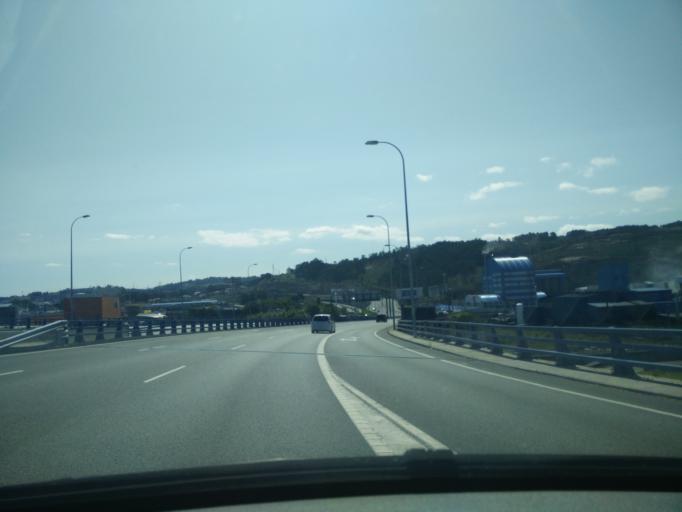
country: ES
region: Galicia
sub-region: Provincia da Coruna
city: A Coruna
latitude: 43.3498
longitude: -8.4340
